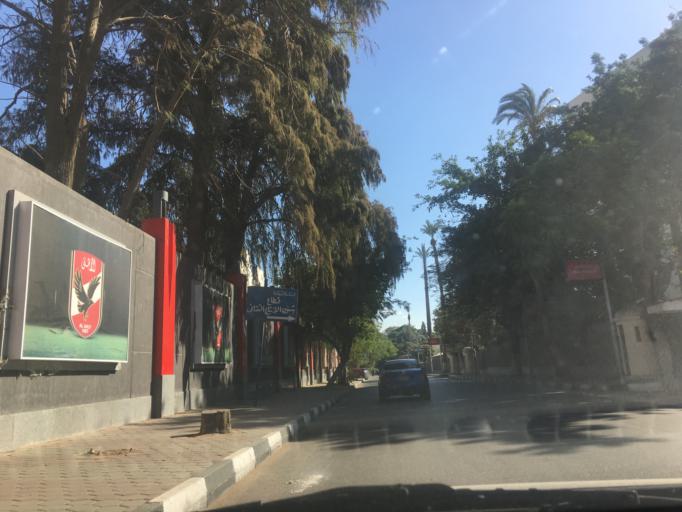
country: EG
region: Muhafazat al Qahirah
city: Cairo
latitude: 30.0442
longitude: 31.2211
